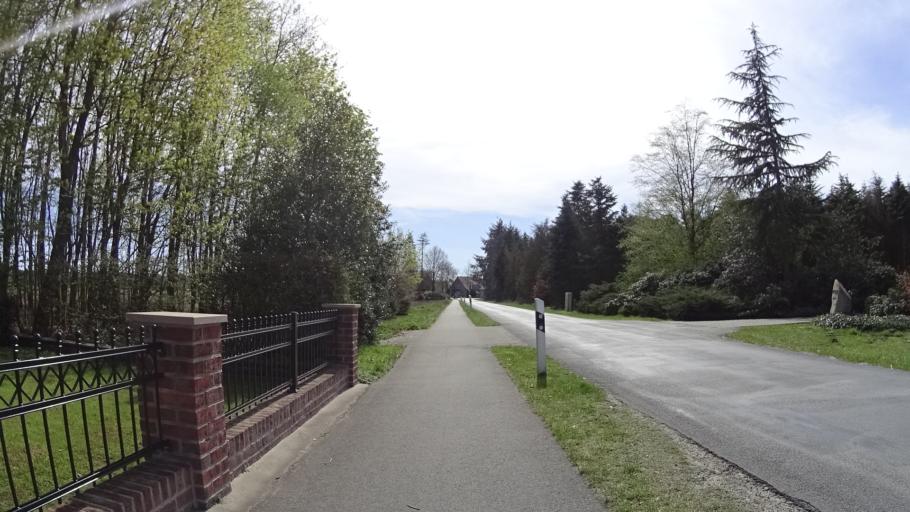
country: DE
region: Lower Saxony
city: Spelle
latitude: 52.3509
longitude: 7.4436
